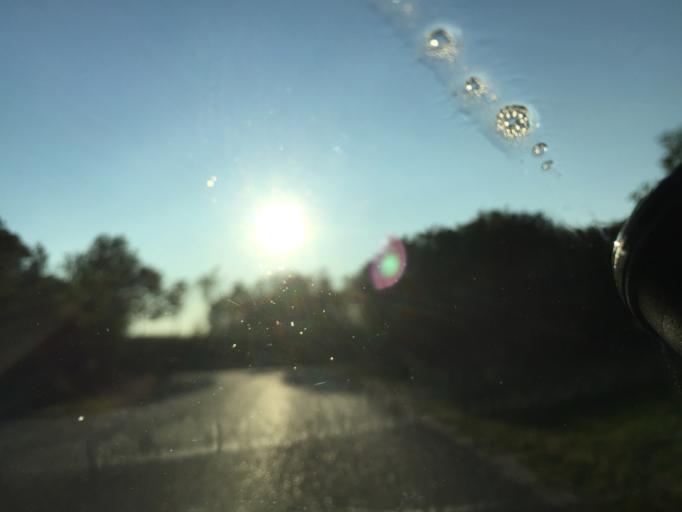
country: DK
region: Central Jutland
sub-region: Silkeborg Kommune
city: Svejbaek
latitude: 56.2235
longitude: 9.6662
